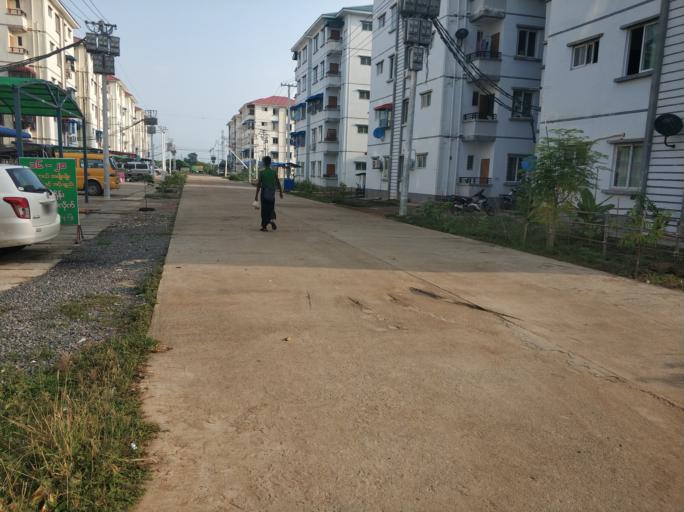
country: MM
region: Mandalay
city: Mandalay
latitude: 21.9160
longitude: 96.1344
